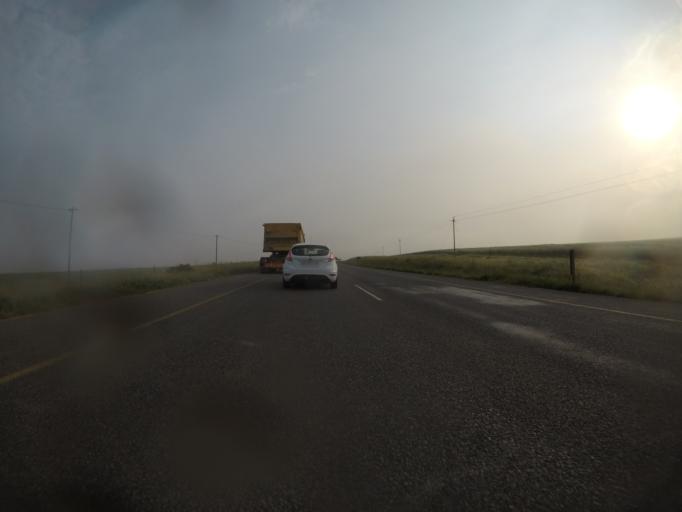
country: ZA
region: Western Cape
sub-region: City of Cape Town
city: Kraaifontein
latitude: -33.6568
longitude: 18.7084
